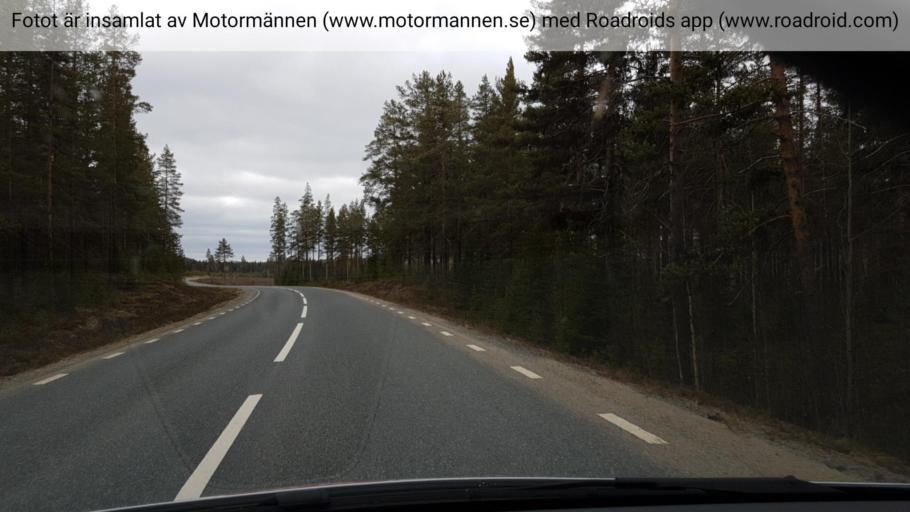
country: SE
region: Vaesternorrland
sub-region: OErnskoeldsviks Kommun
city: Bredbyn
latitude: 63.8390
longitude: 18.4763
